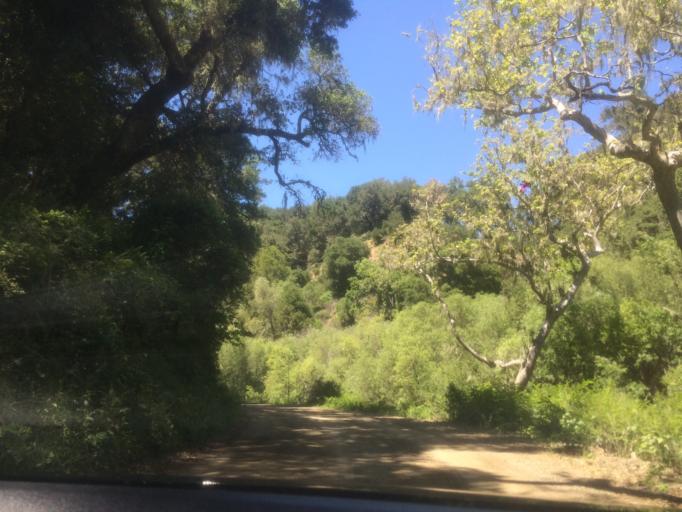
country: US
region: California
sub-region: San Luis Obispo County
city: Templeton
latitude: 35.5249
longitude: -120.7899
